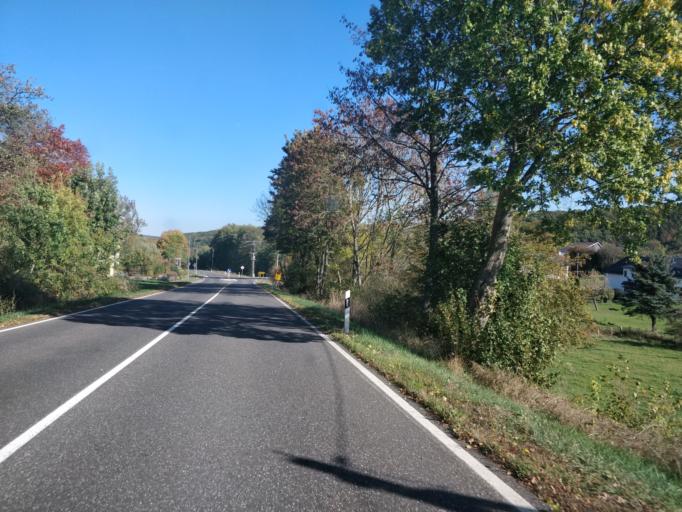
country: DE
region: North Rhine-Westphalia
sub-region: Regierungsbezirk Koln
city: Nettersheim
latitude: 50.5293
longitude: 6.6896
